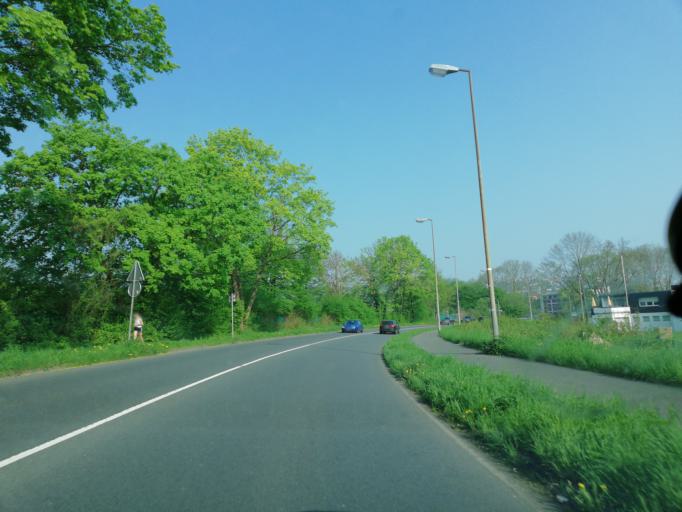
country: DE
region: North Rhine-Westphalia
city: Herdecke
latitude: 51.3927
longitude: 7.4322
